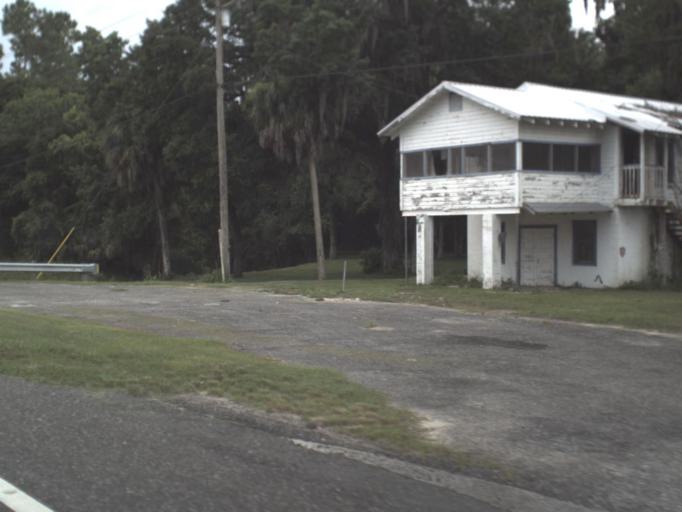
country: US
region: Florida
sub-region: Levy County
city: Bronson
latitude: 29.2761
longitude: -82.7376
